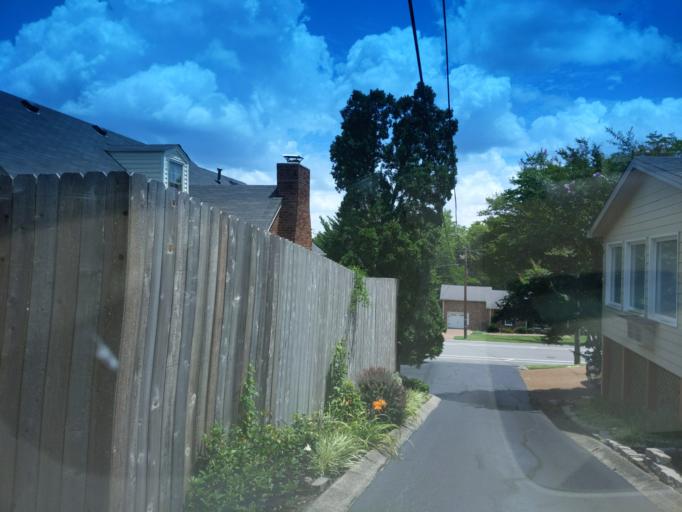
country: US
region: Tennessee
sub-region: Williamson County
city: Brentwood
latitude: 36.0372
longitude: -86.7744
